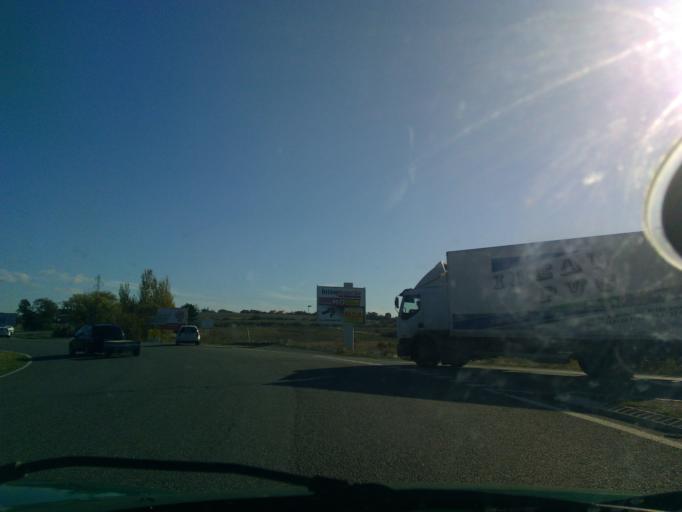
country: FR
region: Languedoc-Roussillon
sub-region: Departement de l'Aude
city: Carcassonne
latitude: 43.2021
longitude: 2.3141
